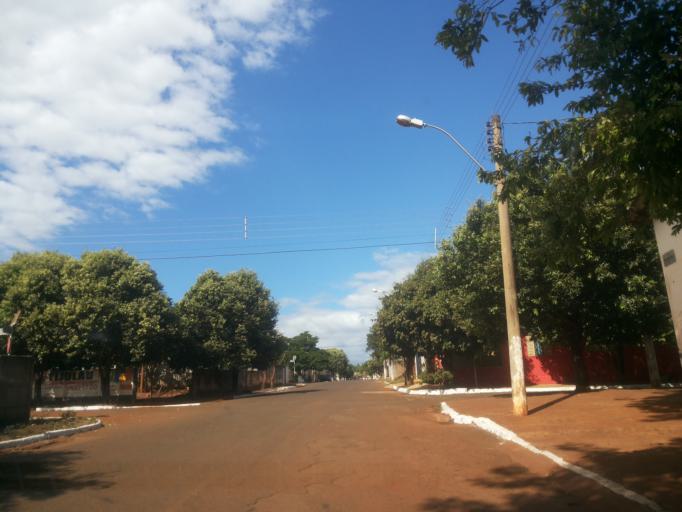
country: BR
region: Goias
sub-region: Itumbiara
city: Itumbiara
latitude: -18.4380
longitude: -49.1870
